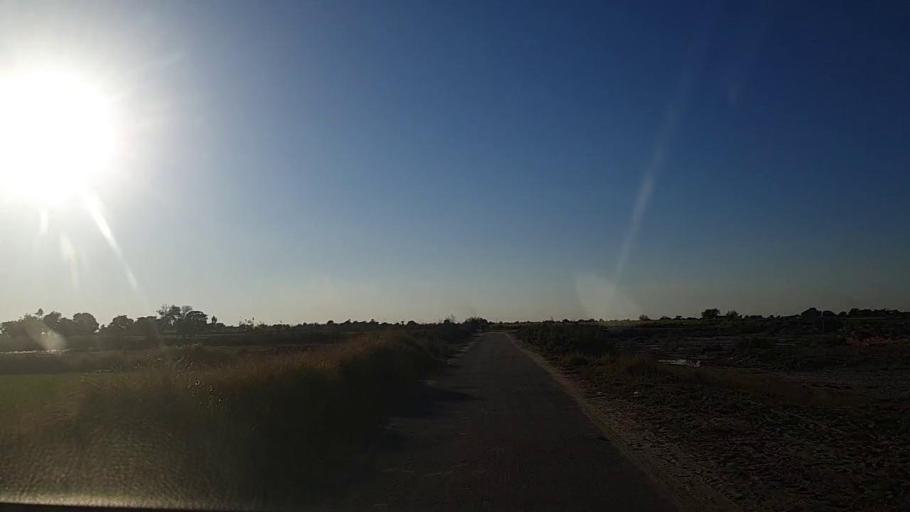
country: PK
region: Sindh
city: Sanghar
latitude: 26.1393
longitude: 68.9280
